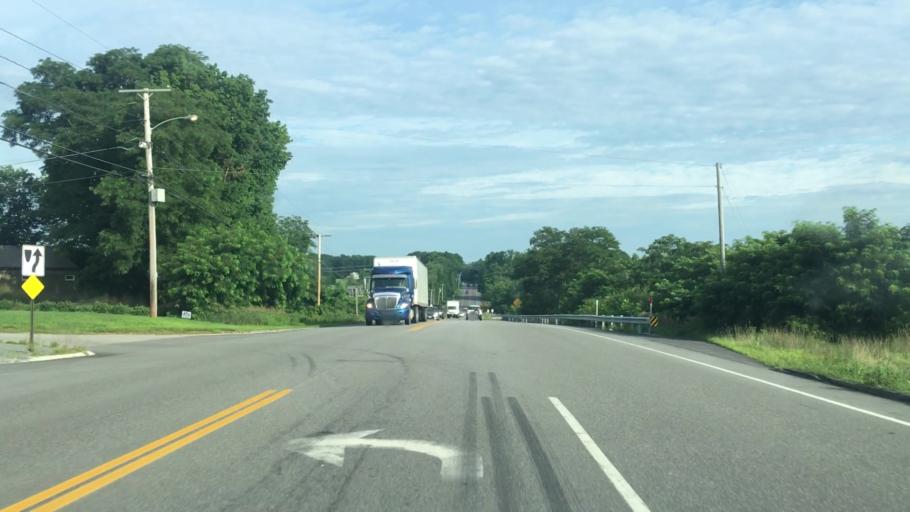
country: US
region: Maine
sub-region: Cumberland County
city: Gorham
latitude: 43.6941
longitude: -70.4922
